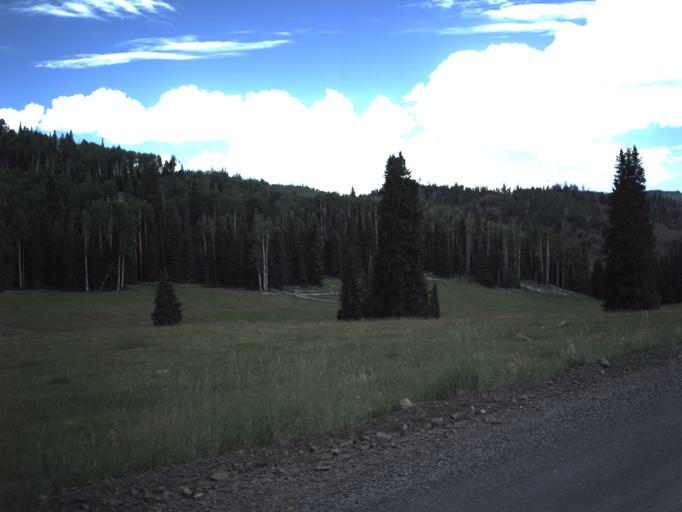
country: US
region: Utah
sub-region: Piute County
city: Junction
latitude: 38.2382
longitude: -112.3588
